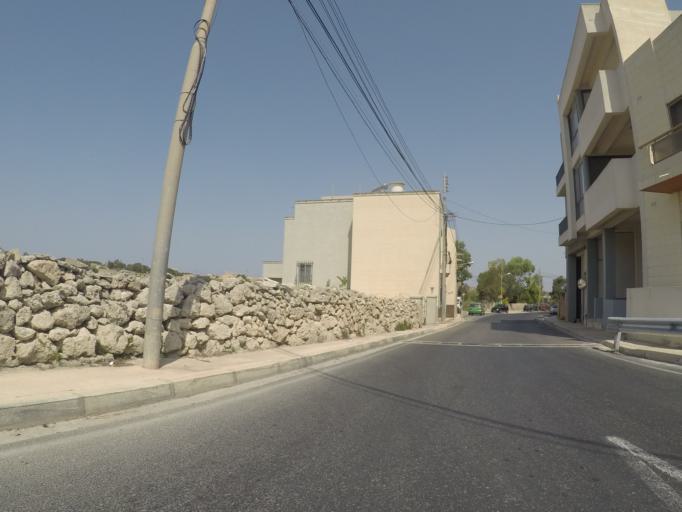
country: MT
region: Ir-Rabat
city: Rabat
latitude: 35.8753
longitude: 14.3961
